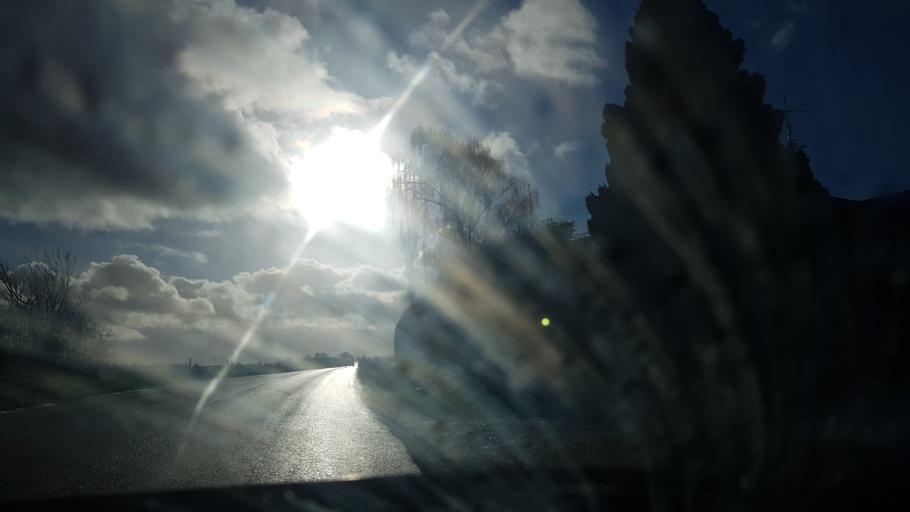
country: DK
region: South Denmark
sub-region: Fredericia Kommune
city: Taulov
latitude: 55.5271
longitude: 9.6395
